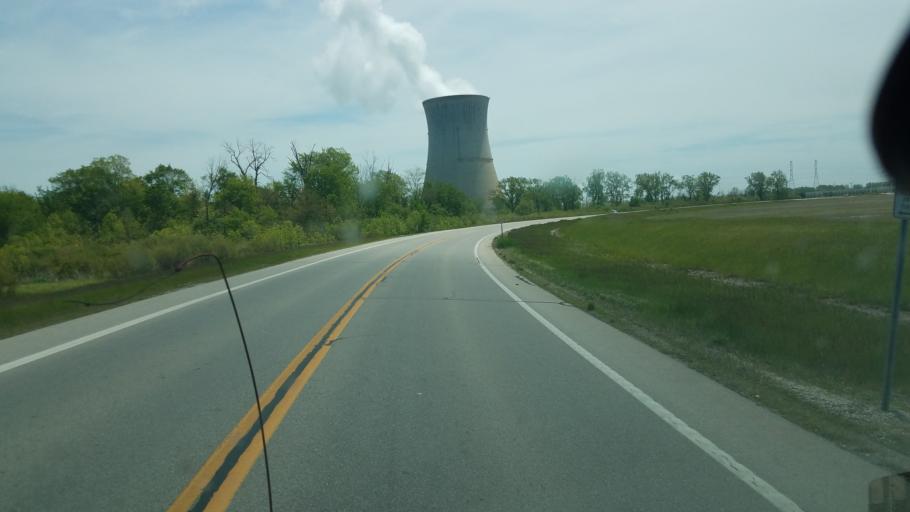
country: US
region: Ohio
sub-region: Ottawa County
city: Oak Harbor
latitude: 41.6032
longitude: -83.1004
